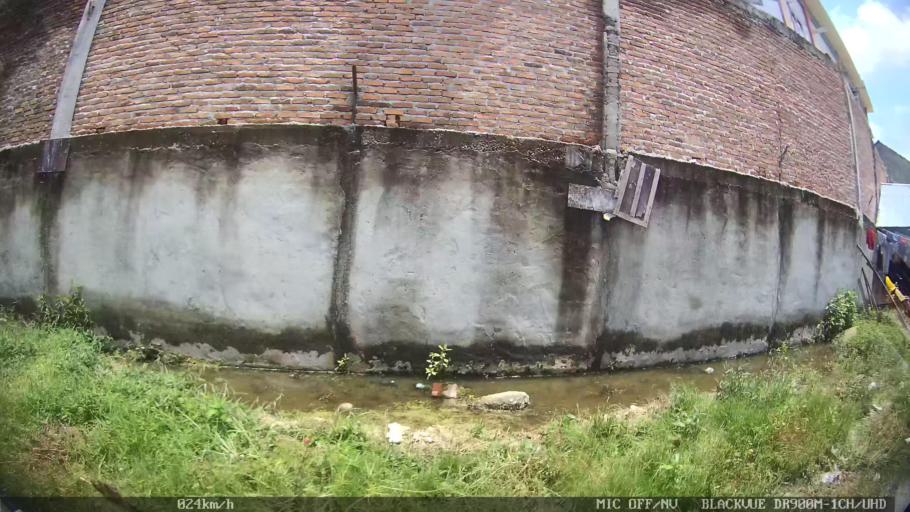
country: ID
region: North Sumatra
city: Percut
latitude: 3.5496
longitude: 98.8529
